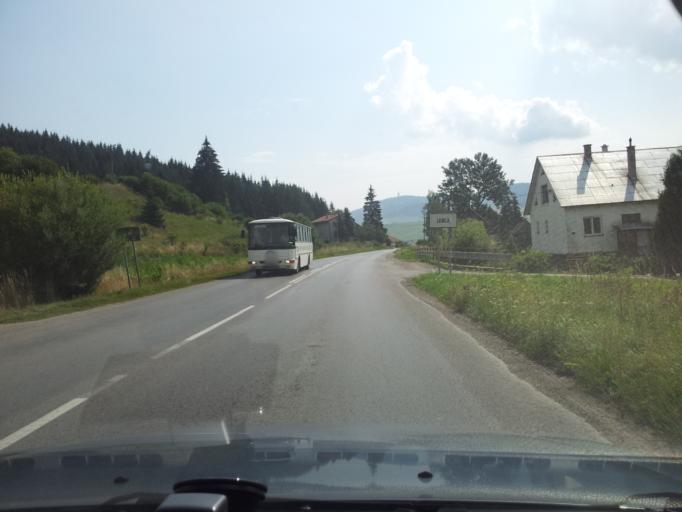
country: SK
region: Zilinsky
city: Namestovo
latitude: 49.3736
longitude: 19.4028
